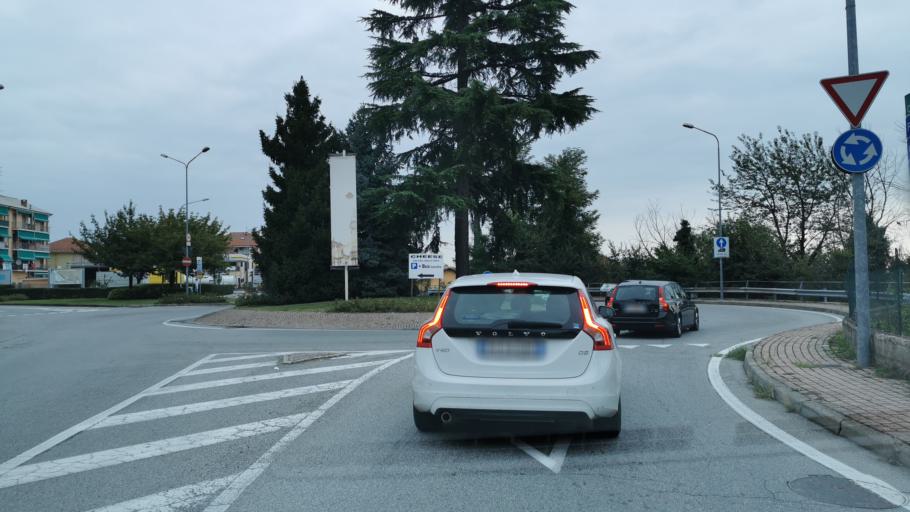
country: IT
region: Piedmont
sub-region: Provincia di Cuneo
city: Bra
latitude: 44.6840
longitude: 7.8497
